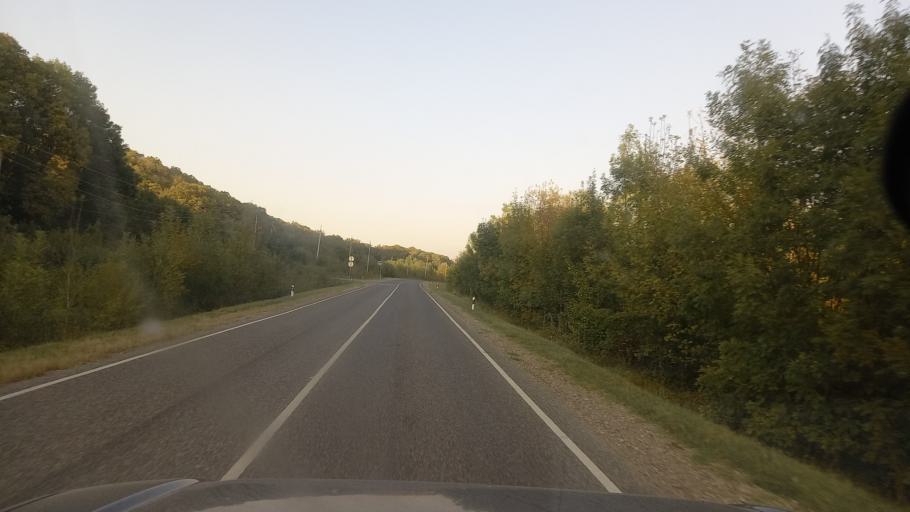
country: RU
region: Krasnodarskiy
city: Smolenskaya
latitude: 44.7456
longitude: 38.7521
